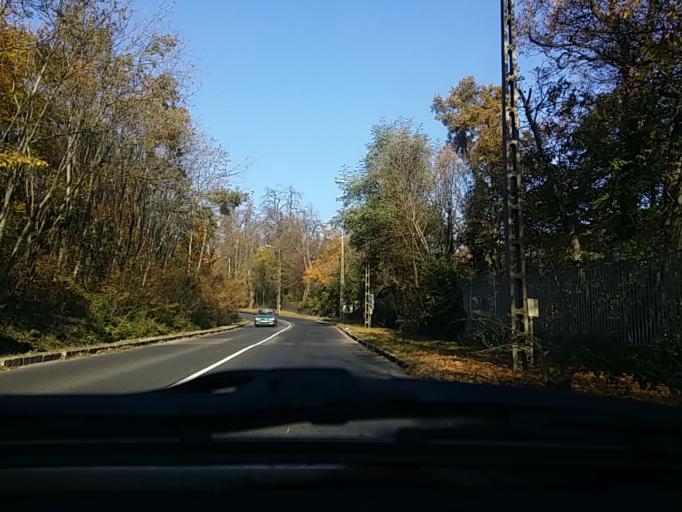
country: HU
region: Pest
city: Budakeszi
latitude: 47.5256
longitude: 18.9566
